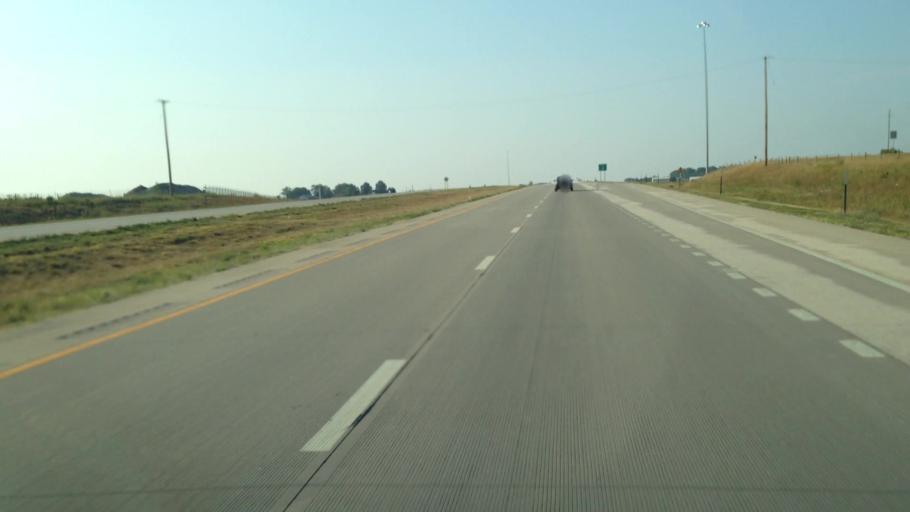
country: US
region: Kansas
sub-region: Douglas County
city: Baldwin City
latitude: 38.7782
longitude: -95.2687
